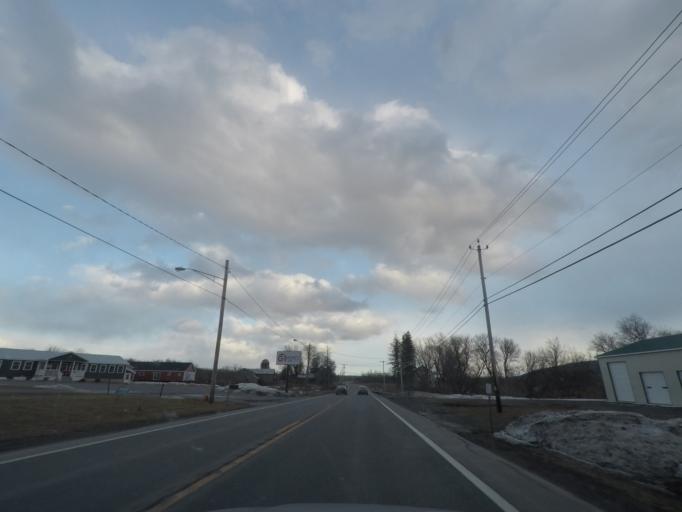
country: US
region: New York
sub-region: Herkimer County
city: Frankfort
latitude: 43.0903
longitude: -75.1310
